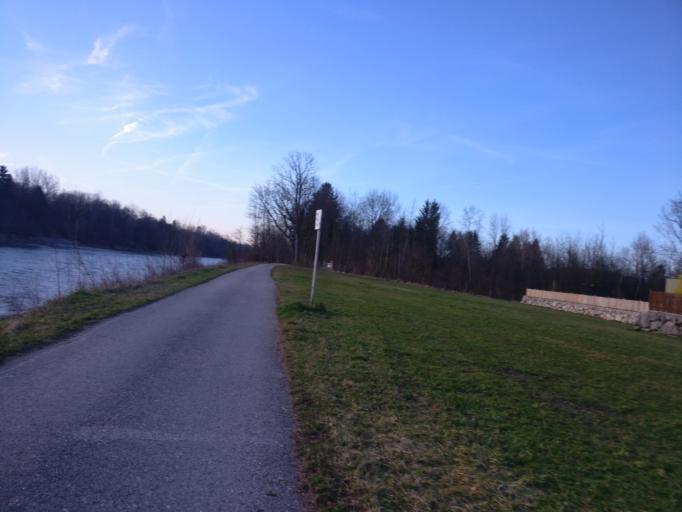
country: DE
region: Bavaria
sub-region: Upper Bavaria
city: Freilassing
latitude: 47.8540
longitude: 13.0031
